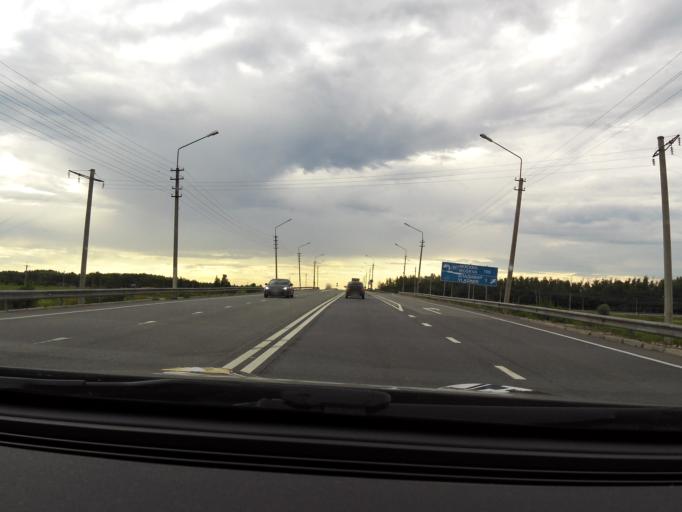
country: RU
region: Vladimir
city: Vorsha
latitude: 56.0789
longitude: 40.2037
